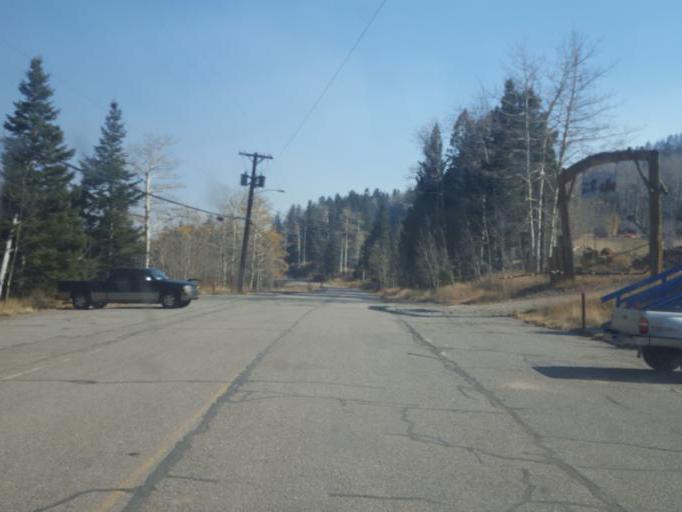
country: US
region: New Mexico
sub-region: Los Alamos County
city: Los Alamos
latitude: 35.8951
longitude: -106.3906
